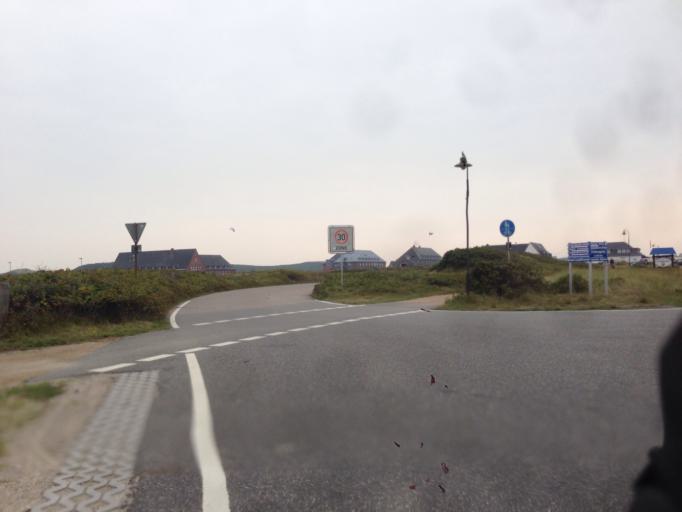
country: DE
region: Schleswig-Holstein
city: Norddorf
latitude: 54.7725
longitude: 8.2860
